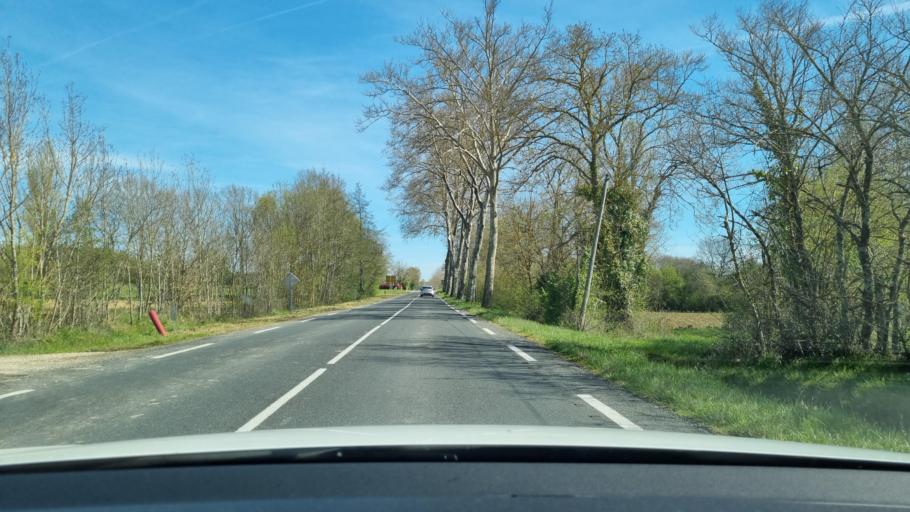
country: FR
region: Midi-Pyrenees
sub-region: Departement du Gers
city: Lombez
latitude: 43.4031
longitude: 0.7974
